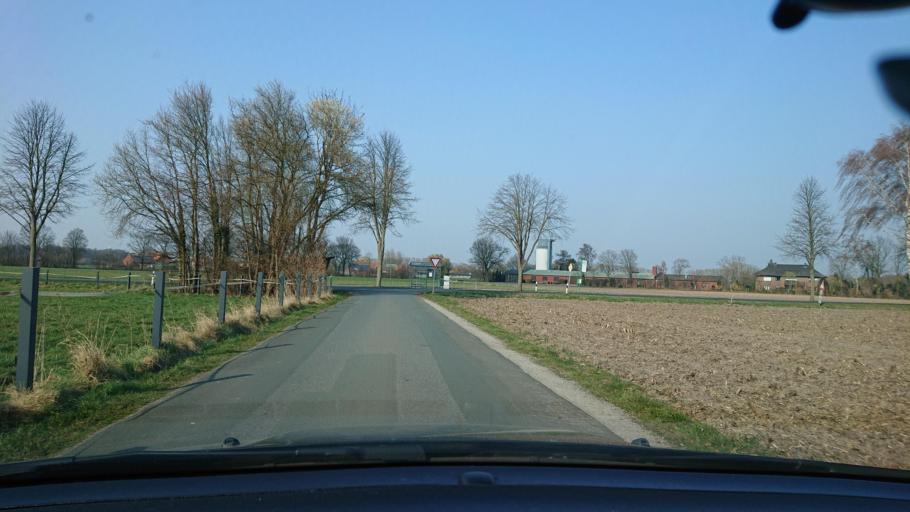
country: DE
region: North Rhine-Westphalia
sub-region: Regierungsbezirk Detmold
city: Langenberg
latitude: 51.7721
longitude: 8.3711
